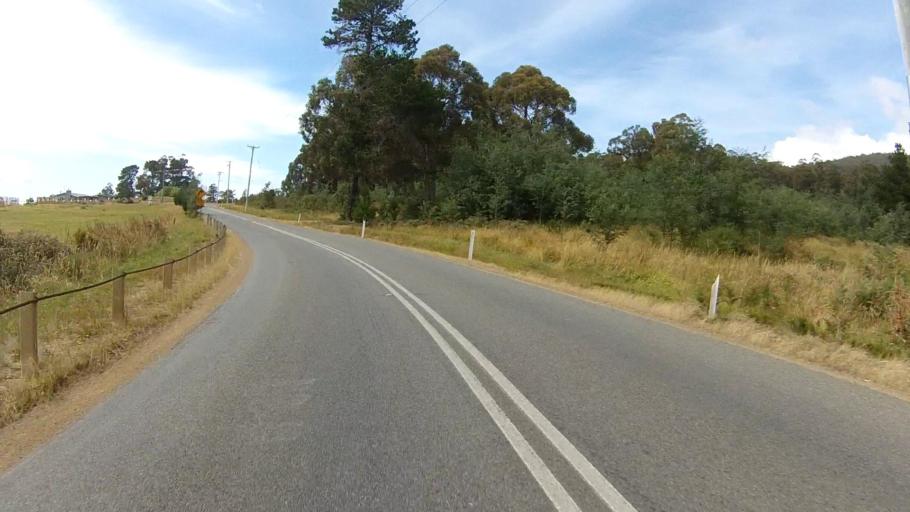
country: AU
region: Tasmania
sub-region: Kingborough
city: Kettering
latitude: -43.1910
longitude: 147.2458
